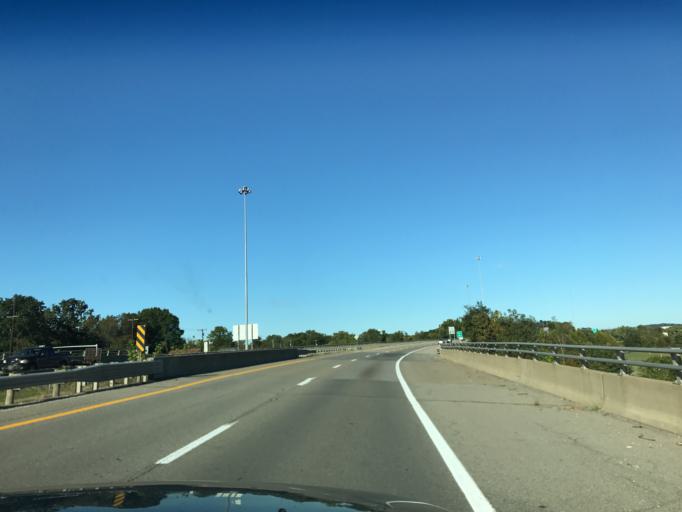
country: US
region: West Virginia
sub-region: Wood County
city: Parkersburg
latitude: 39.2542
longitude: -81.5406
